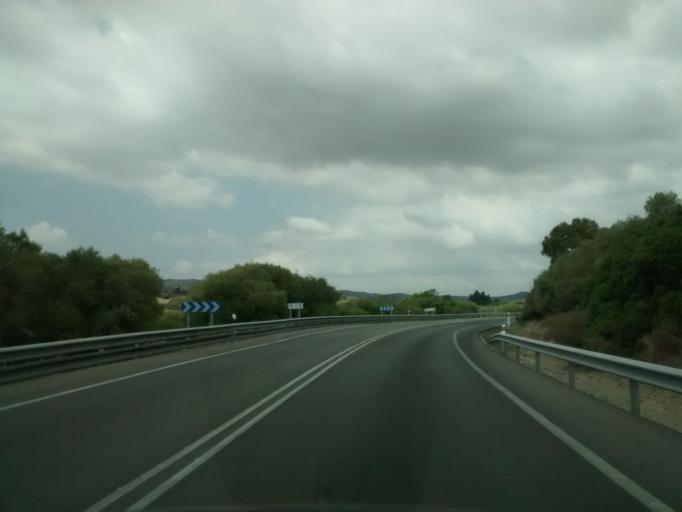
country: ES
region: Andalusia
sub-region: Provincia de Cadiz
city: Tarifa
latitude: 36.0919
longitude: -5.6961
